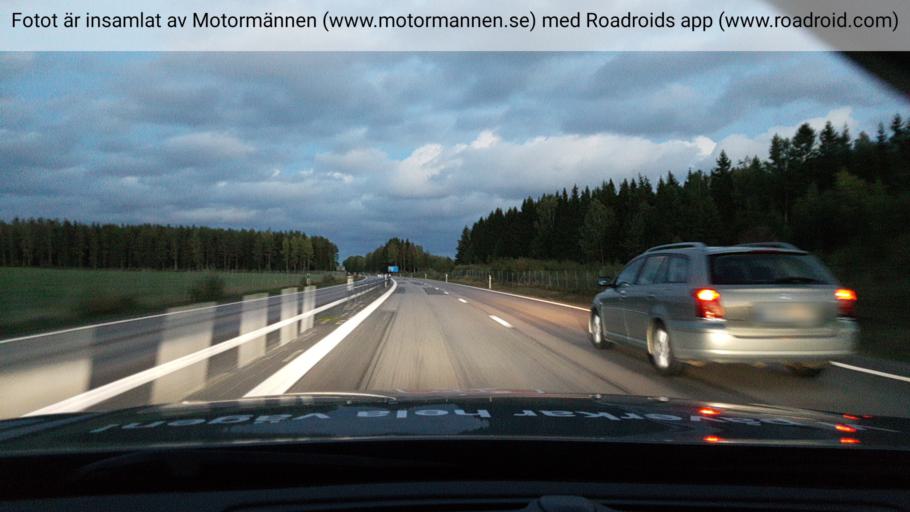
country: SE
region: Vaermland
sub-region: Kristinehamns Kommun
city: Kristinehamn
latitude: 59.3815
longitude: 13.8876
